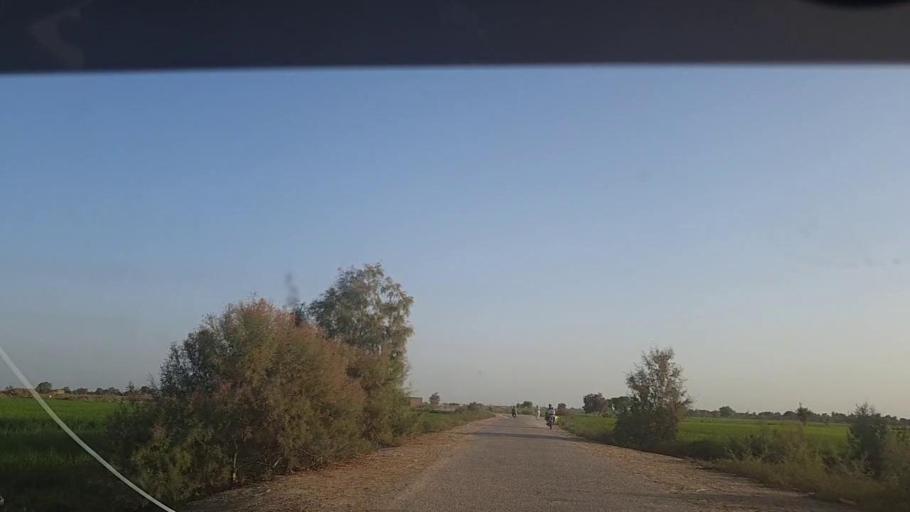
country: PK
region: Sindh
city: Thul
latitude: 28.1520
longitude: 68.8864
